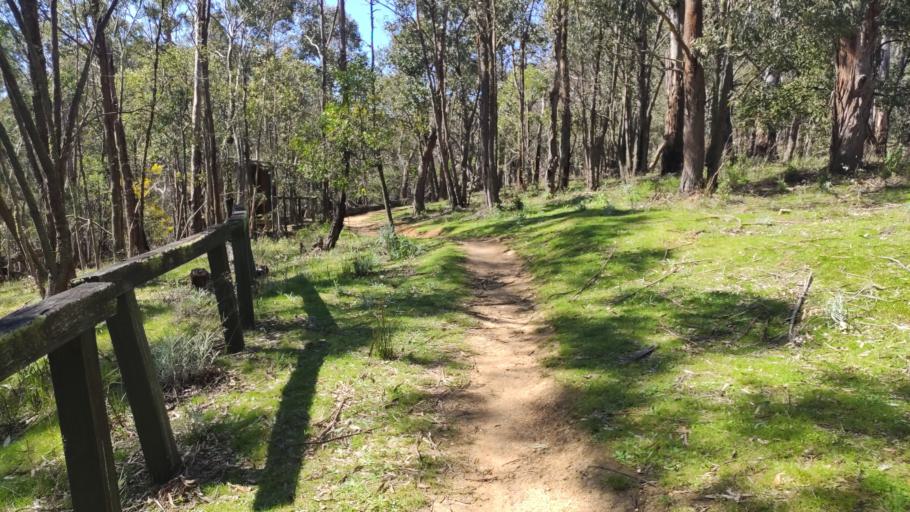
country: AU
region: Victoria
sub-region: Ballarat North
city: Delacombe
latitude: -37.7701
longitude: 143.7387
